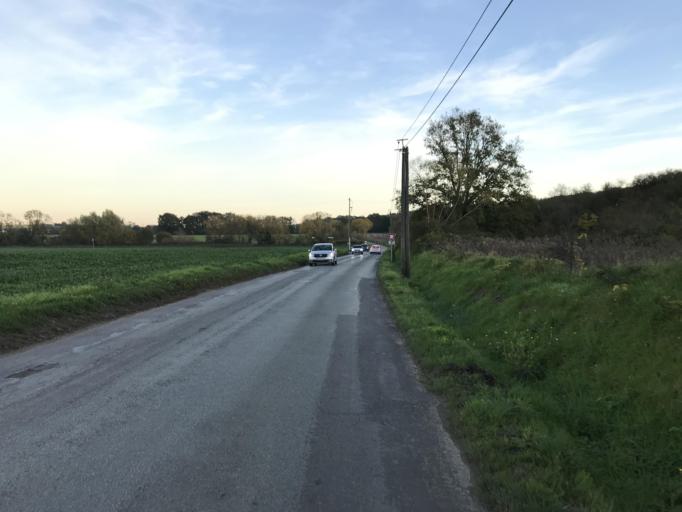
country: FR
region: Ile-de-France
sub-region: Departement de l'Essonne
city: Saulx-les-Chartreux
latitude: 48.6833
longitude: 2.2604
